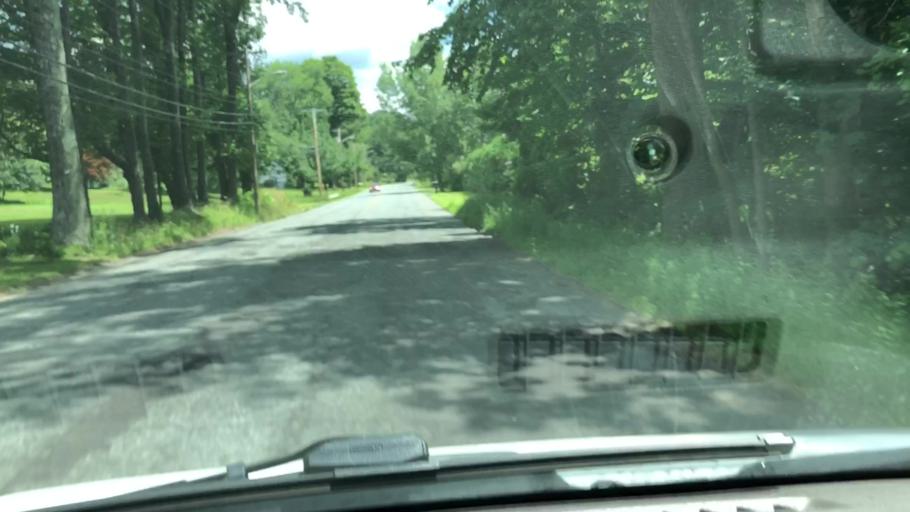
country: US
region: Massachusetts
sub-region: Berkshire County
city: Adams
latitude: 42.5853
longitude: -73.1027
